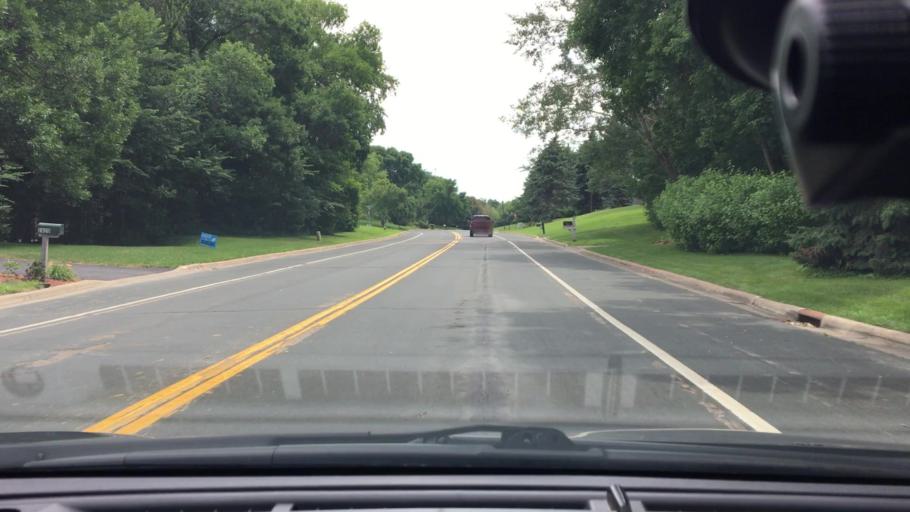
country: US
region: Minnesota
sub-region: Hennepin County
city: New Hope
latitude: 45.0116
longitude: -93.4130
